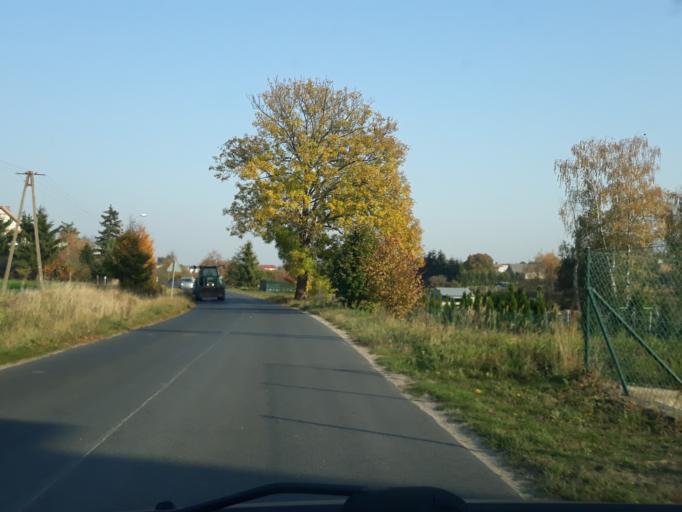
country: PL
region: Kujawsko-Pomorskie
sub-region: Powiat sepolenski
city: Sepolno Krajenskie
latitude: 53.4660
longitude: 17.5202
